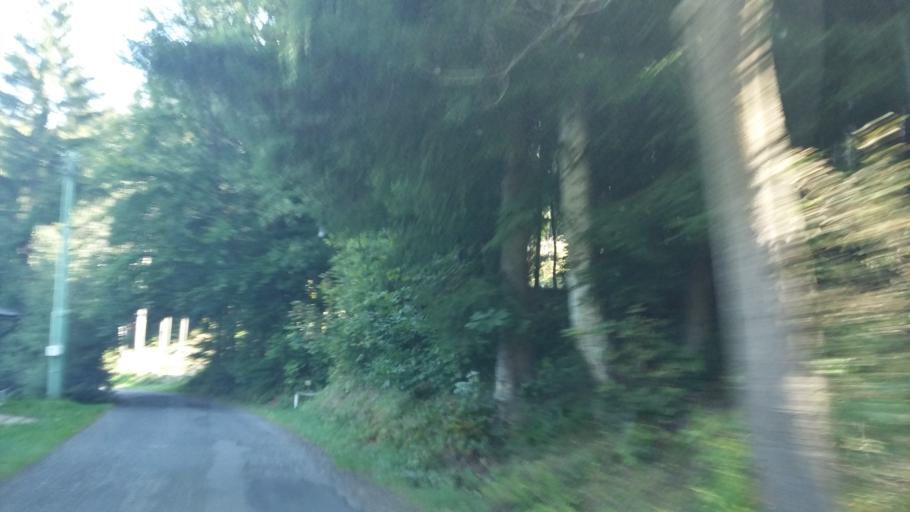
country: CZ
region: Liberecky
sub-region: Okres Jablonec nad Nisou
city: Janov nad Nisou
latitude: 50.7615
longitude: 15.1838
